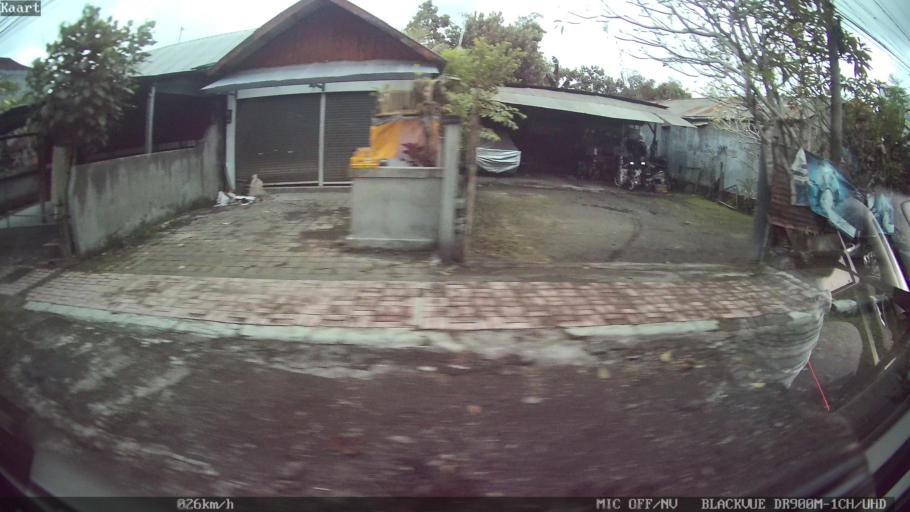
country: ID
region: Bali
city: Banjar Mambalkajanan
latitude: -8.5535
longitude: 115.2193
